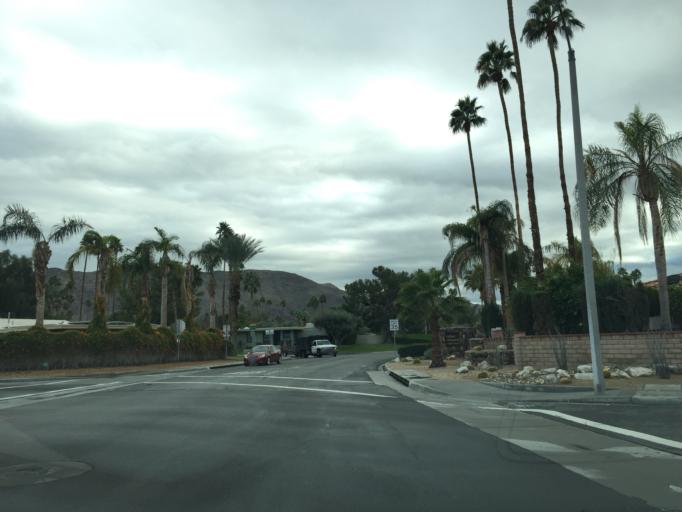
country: US
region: California
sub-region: Riverside County
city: Palm Springs
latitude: 33.7942
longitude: -116.5373
